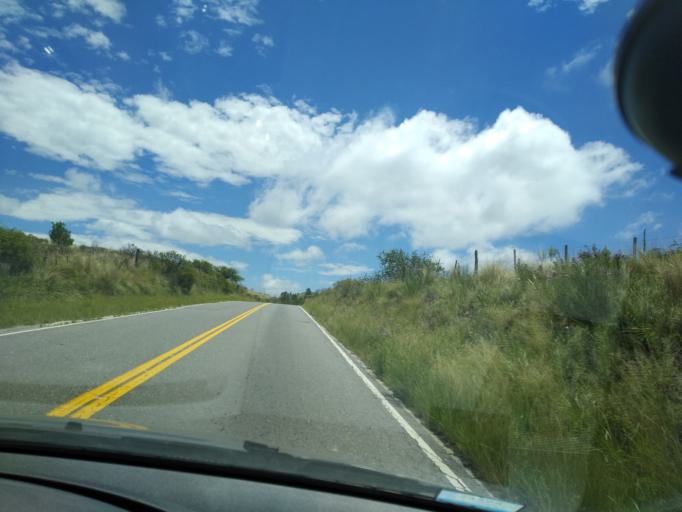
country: AR
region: Cordoba
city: Cuesta Blanca
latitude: -31.5991
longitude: -64.5435
